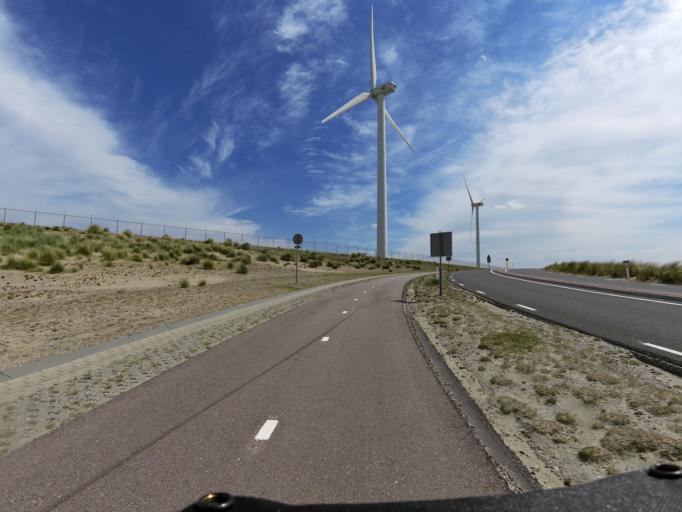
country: NL
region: South Holland
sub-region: Gemeente Goeree-Overflakkee
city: Goedereede
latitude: 51.9226
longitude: 3.9897
